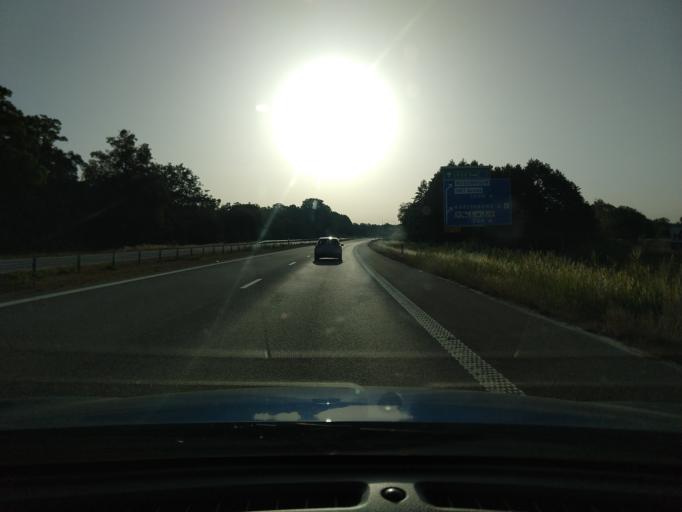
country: SE
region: Blekinge
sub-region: Karlskrona Kommun
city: Rodeby
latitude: 56.2134
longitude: 15.5822
